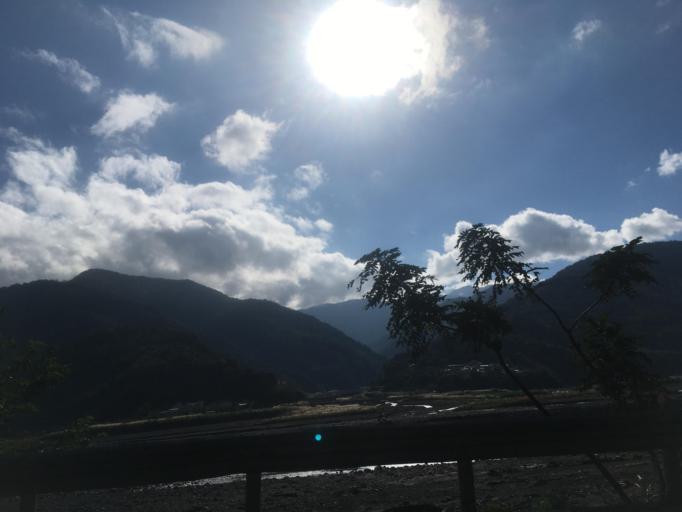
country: TW
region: Taiwan
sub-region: Yilan
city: Yilan
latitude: 24.6085
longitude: 121.5250
